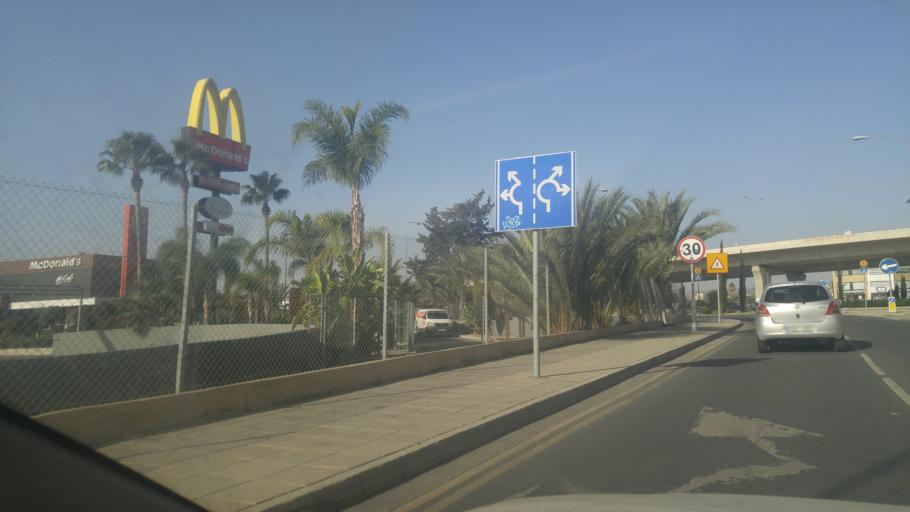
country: CY
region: Limassol
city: Pano Polemidia
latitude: 34.6887
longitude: 33.0099
